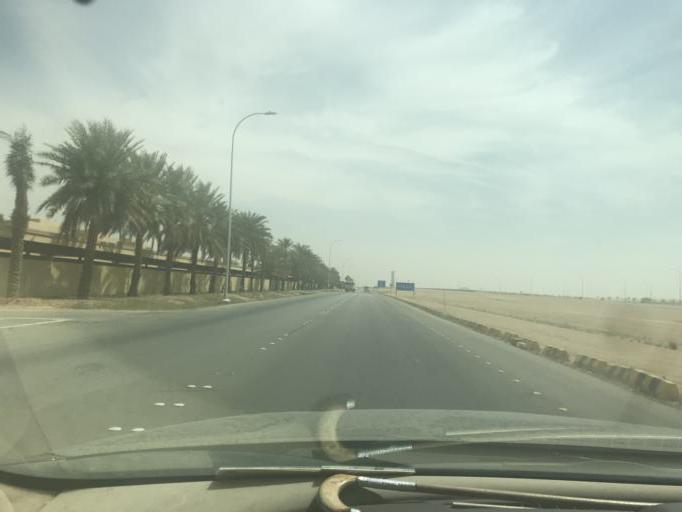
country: SA
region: Ar Riyad
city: Riyadh
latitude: 24.9769
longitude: 46.6879
